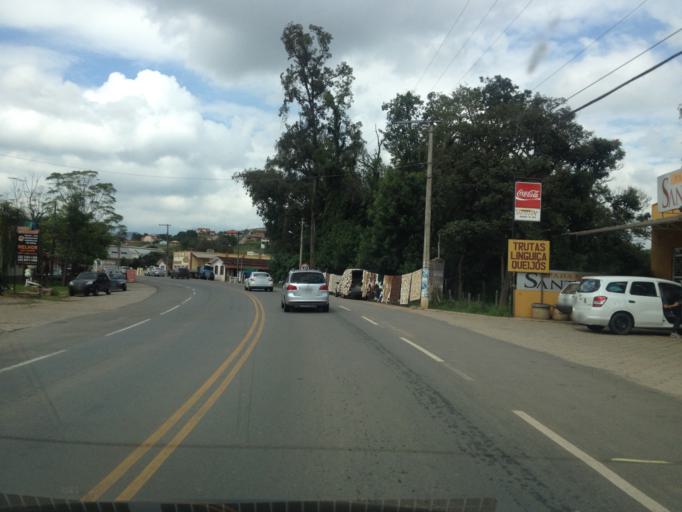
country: BR
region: Minas Gerais
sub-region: Itanhandu
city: Itanhandu
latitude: -22.2503
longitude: -44.9352
